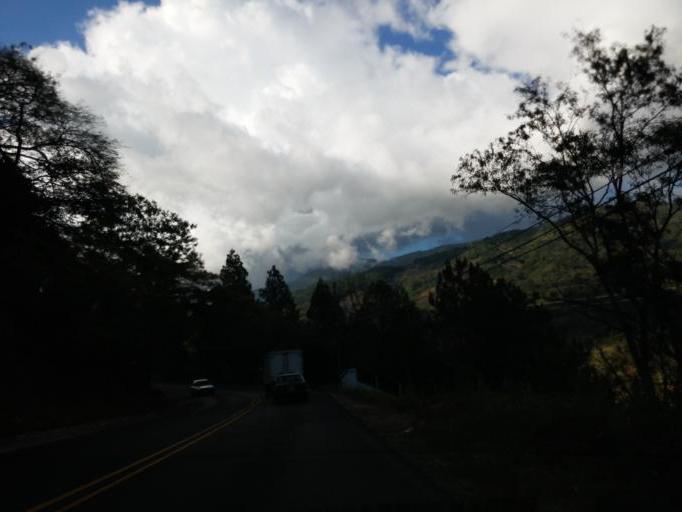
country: CR
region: San Jose
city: San Ignacio
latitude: 9.7965
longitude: -84.1568
